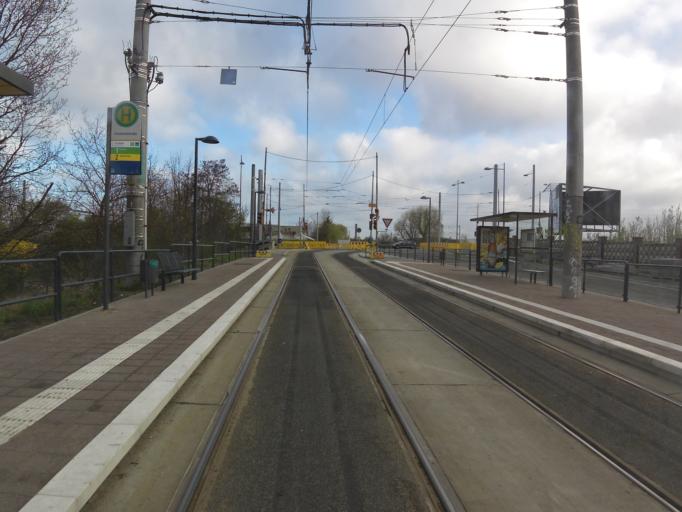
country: DE
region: Saxony
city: Leipzig
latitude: 51.3199
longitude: 12.3176
